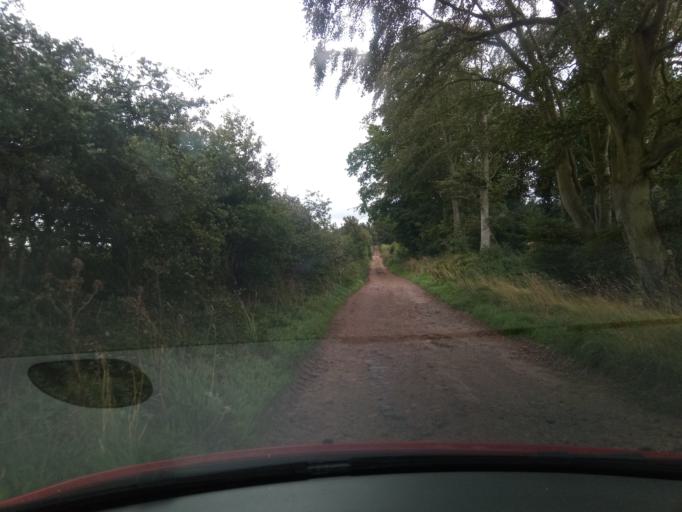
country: GB
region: Scotland
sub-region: The Scottish Borders
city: Jedburgh
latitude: 55.4885
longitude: -2.5222
